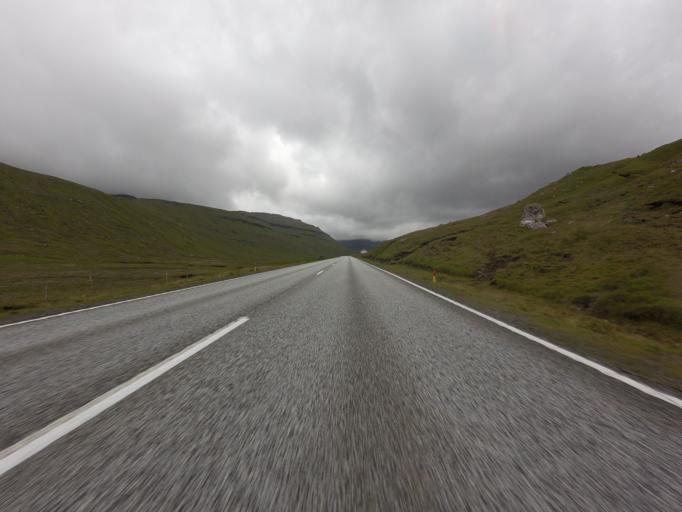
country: FO
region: Streymoy
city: Kollafjordhur
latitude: 62.1222
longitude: -6.9907
